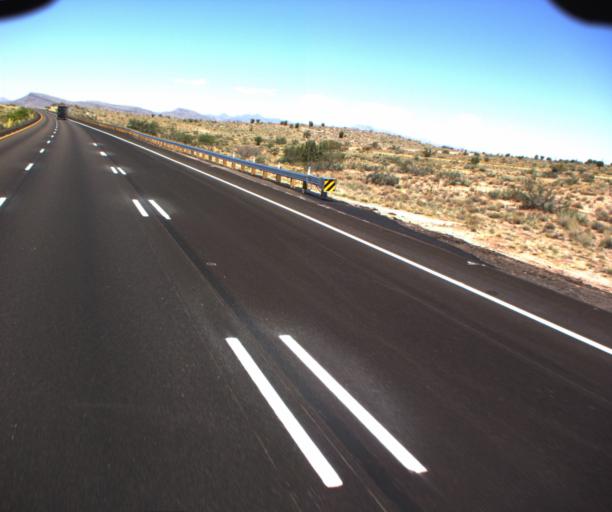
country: US
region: Arizona
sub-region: Mohave County
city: Peach Springs
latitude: 35.1612
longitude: -113.5722
